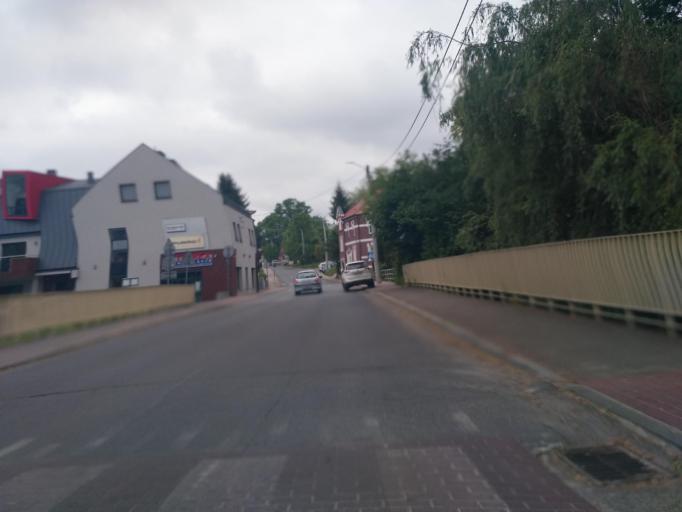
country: PL
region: Subcarpathian Voivodeship
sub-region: Krosno
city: Krosno
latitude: 49.6915
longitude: 21.7640
